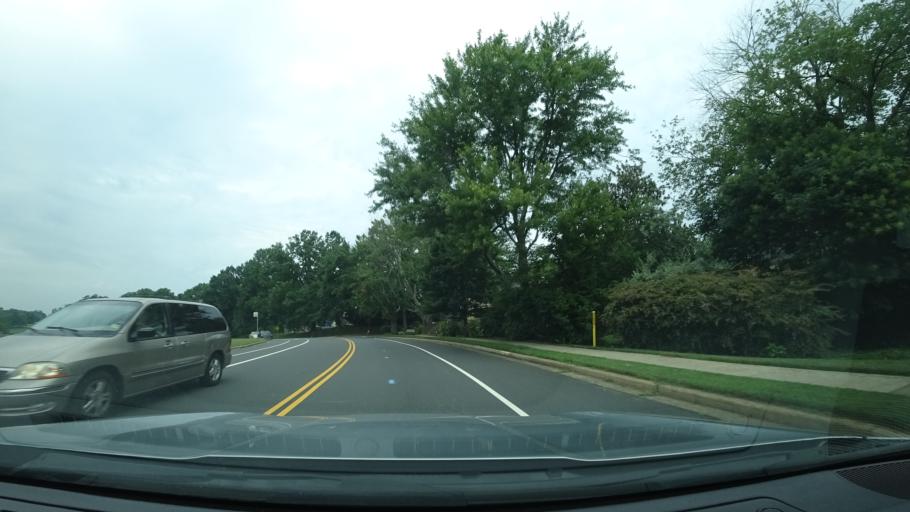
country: US
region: Virginia
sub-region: Fairfax County
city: Reston
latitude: 38.9585
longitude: -77.3374
